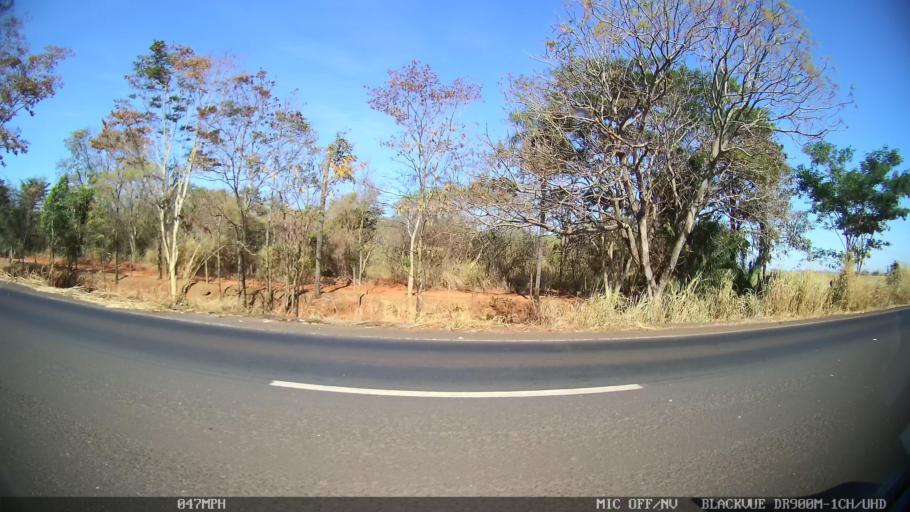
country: BR
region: Sao Paulo
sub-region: Barretos
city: Barretos
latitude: -20.5759
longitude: -48.6805
